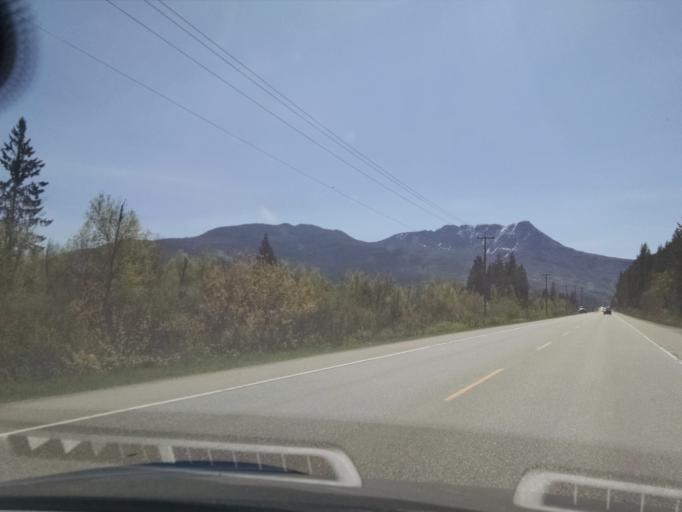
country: CA
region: British Columbia
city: Salmon Arm
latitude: 50.7238
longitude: -119.3170
